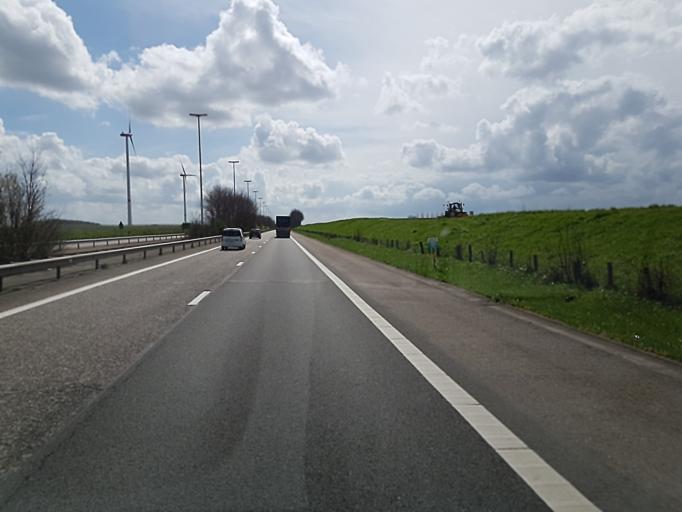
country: BE
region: Flanders
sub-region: Provincie Limburg
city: Hoeselt
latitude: 50.8174
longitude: 5.5145
